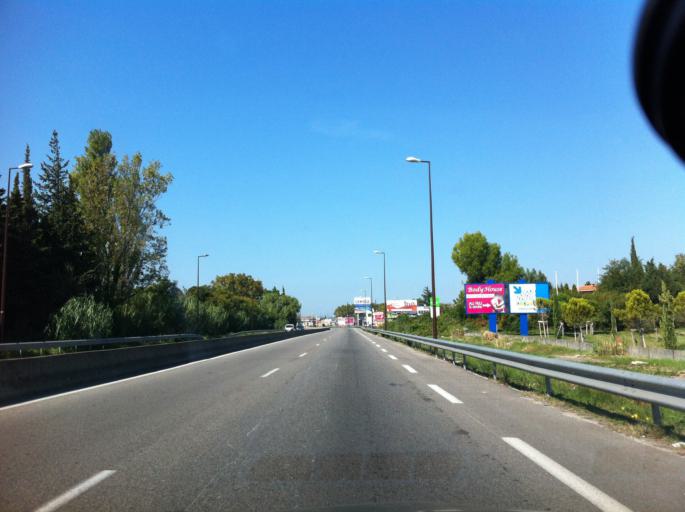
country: FR
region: Provence-Alpes-Cote d'Azur
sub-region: Departement du Vaucluse
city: Montfavet
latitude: 43.9230
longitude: 4.8556
